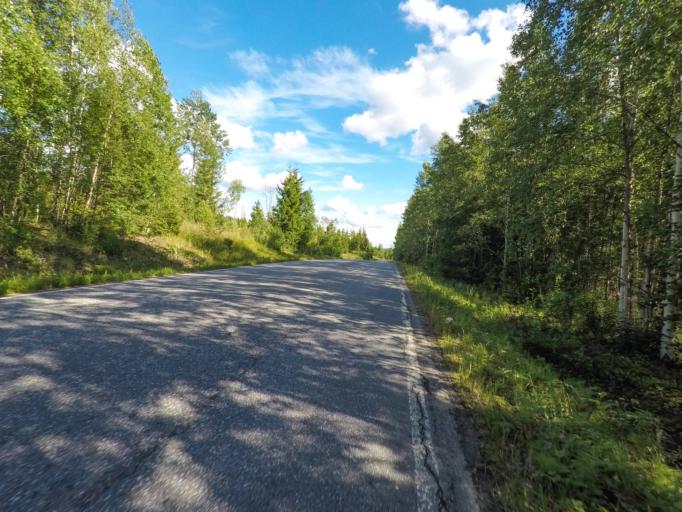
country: FI
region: South Karelia
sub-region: Imatra
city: Imatra
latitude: 61.1311
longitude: 28.6617
